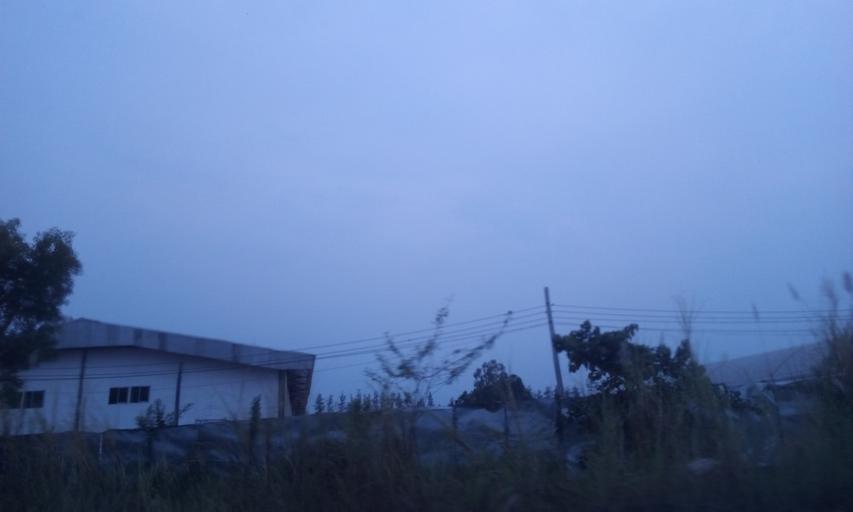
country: TH
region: Chachoengsao
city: Ban Pho
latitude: 13.5989
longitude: 101.1759
